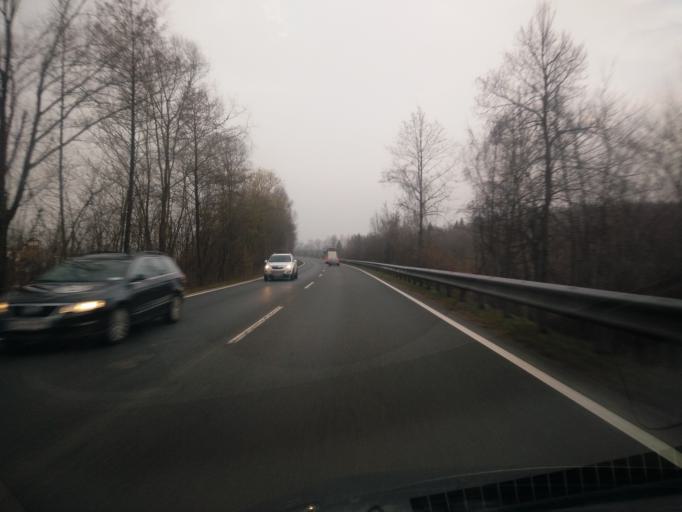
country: DE
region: Bavaria
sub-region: Upper Bavaria
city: Laufen
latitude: 47.9197
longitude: 12.9738
